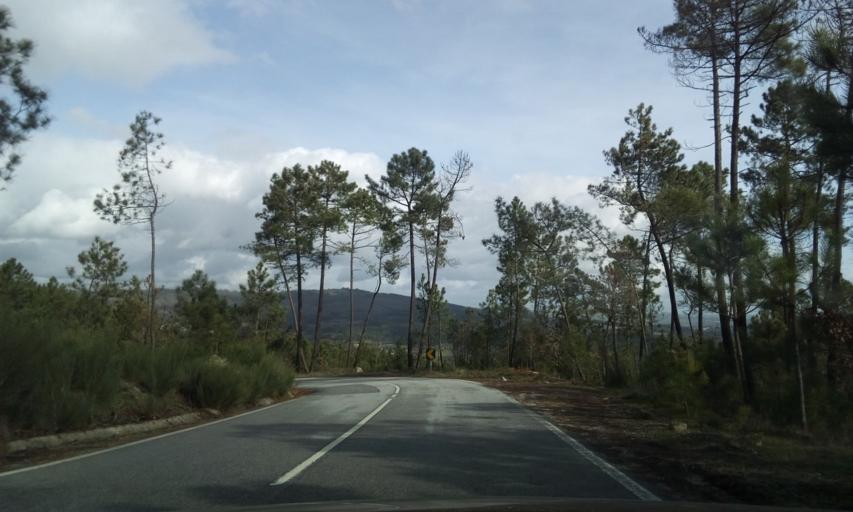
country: PT
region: Guarda
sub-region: Fornos de Algodres
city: Fornos de Algodres
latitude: 40.6609
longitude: -7.6394
